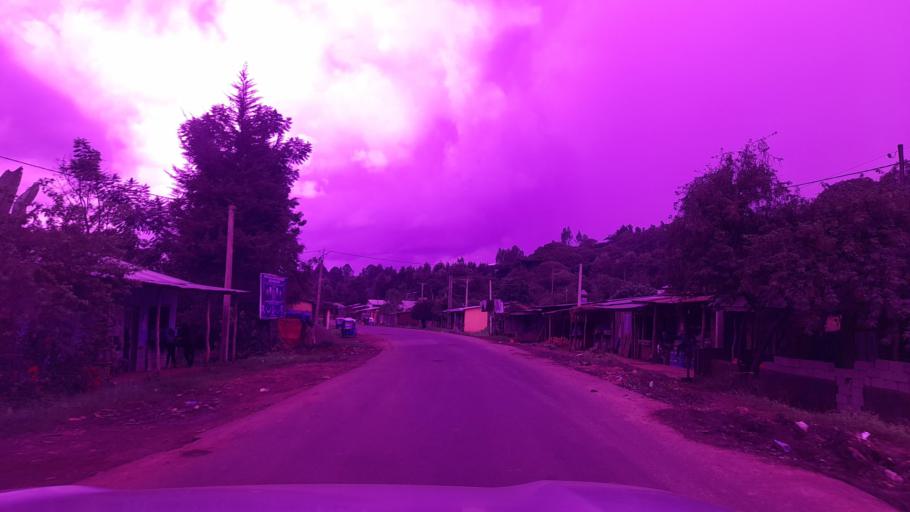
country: ET
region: Oromiya
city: Jima
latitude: 7.6672
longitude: 36.8916
